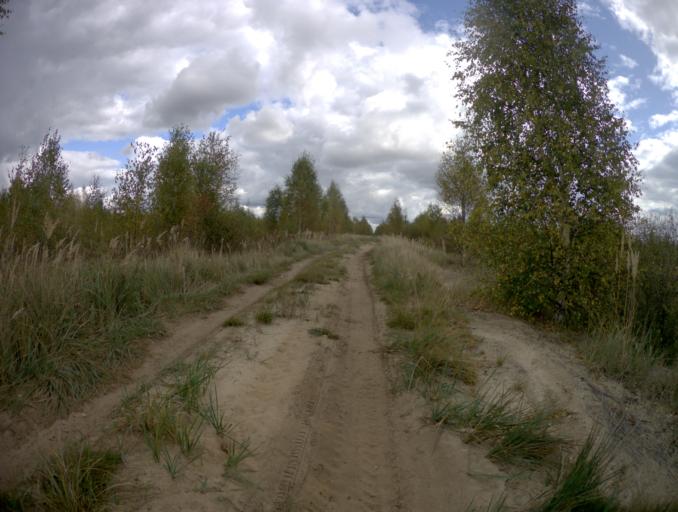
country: RU
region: Vladimir
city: Urshel'skiy
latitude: 55.7690
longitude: 40.1253
